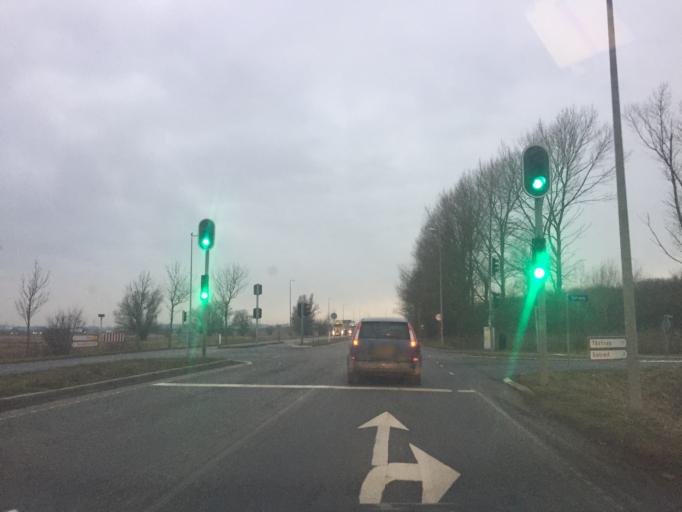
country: DK
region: Zealand
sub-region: Solrod Kommune
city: Solrod
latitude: 55.5150
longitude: 12.1975
